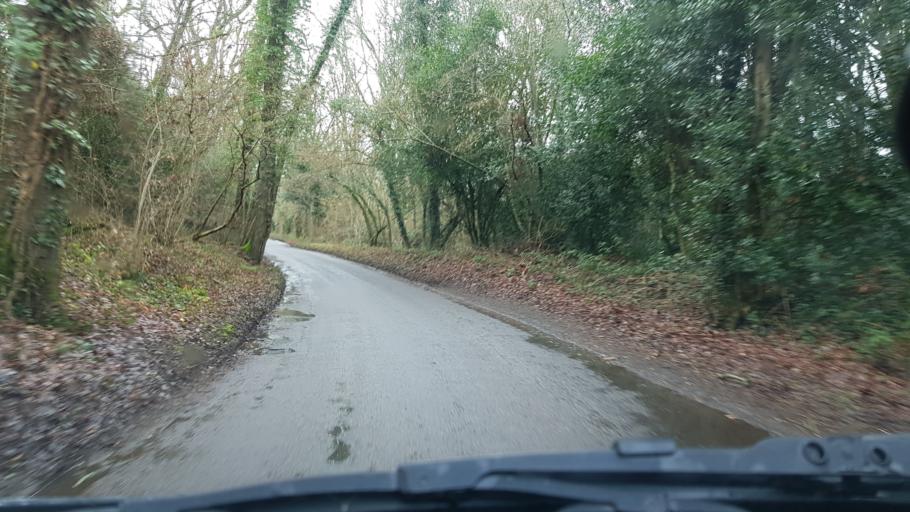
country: GB
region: England
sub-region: Surrey
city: Chiddingfold
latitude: 51.1145
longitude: -0.6556
